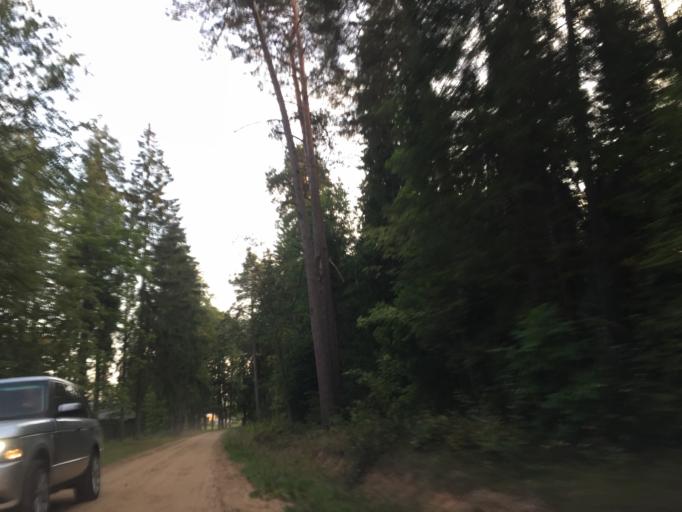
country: LV
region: Baldone
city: Baldone
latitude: 56.7492
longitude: 24.4001
